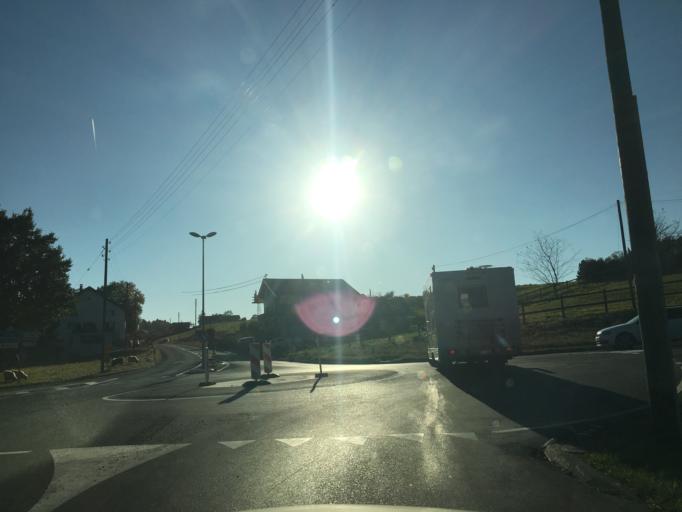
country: CH
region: Vaud
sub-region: Lavaux-Oron District
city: Savigny
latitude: 46.5340
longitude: 6.7565
